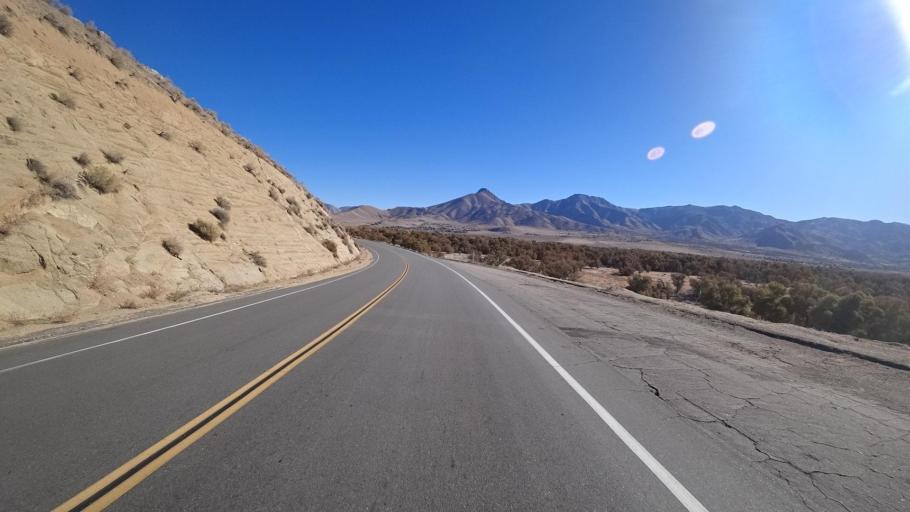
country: US
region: California
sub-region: Kern County
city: Weldon
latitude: 35.6737
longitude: -118.3553
